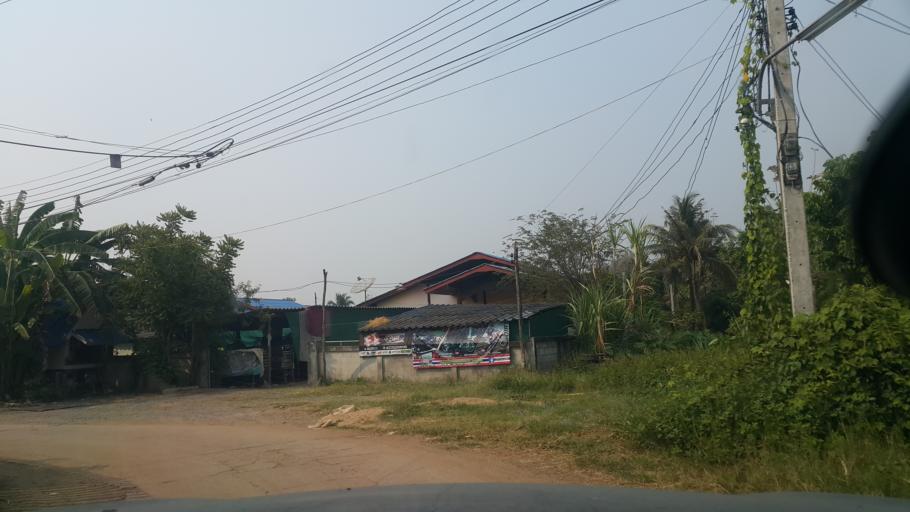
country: TH
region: Chiang Mai
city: Mae On
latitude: 18.7624
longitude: 99.2603
